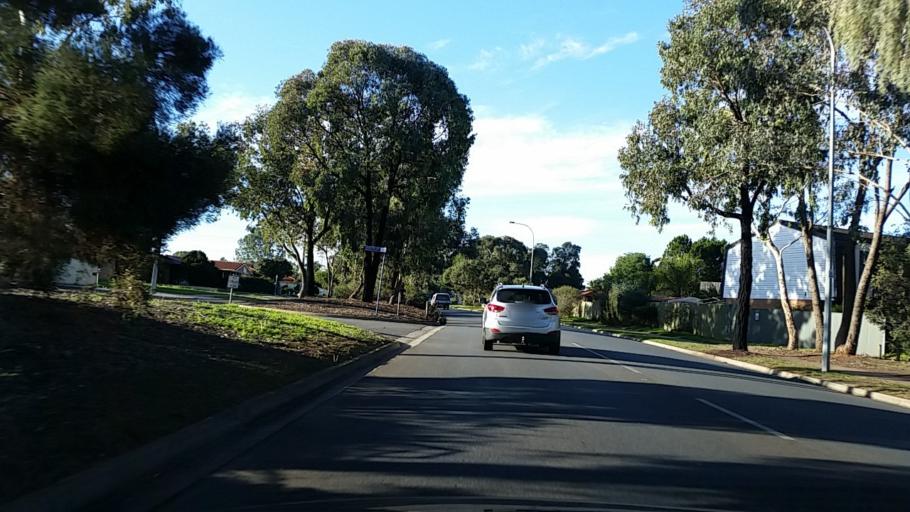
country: AU
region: South Australia
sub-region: Salisbury
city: Salisbury
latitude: -34.7765
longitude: 138.6131
